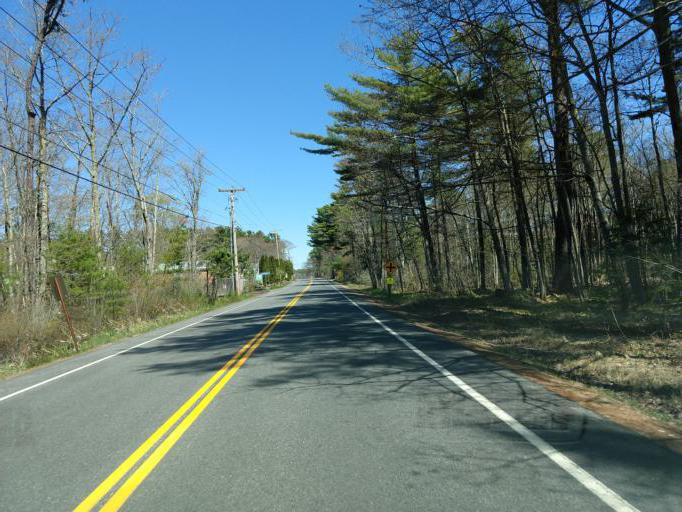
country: US
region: Maine
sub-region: York County
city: Kennebunk
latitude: 43.3507
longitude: -70.5255
